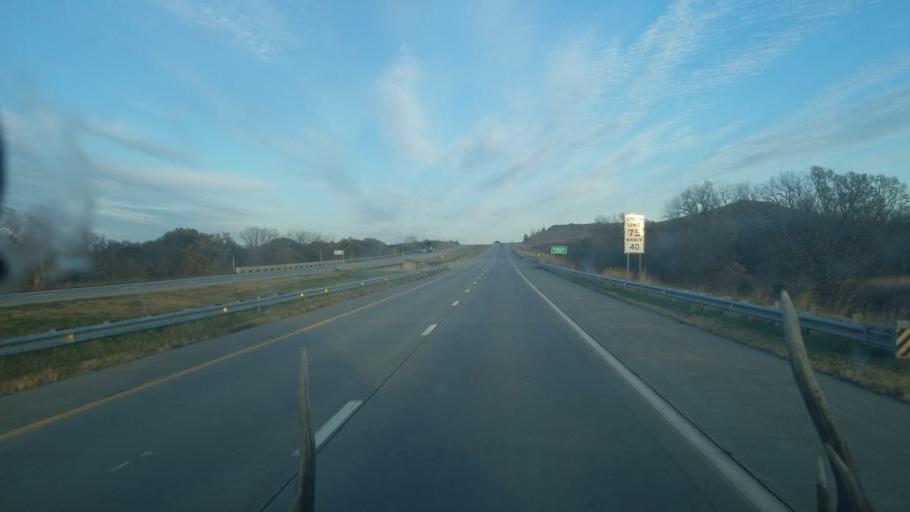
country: US
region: Kansas
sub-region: Riley County
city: Ogden
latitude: 39.0670
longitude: -96.6464
